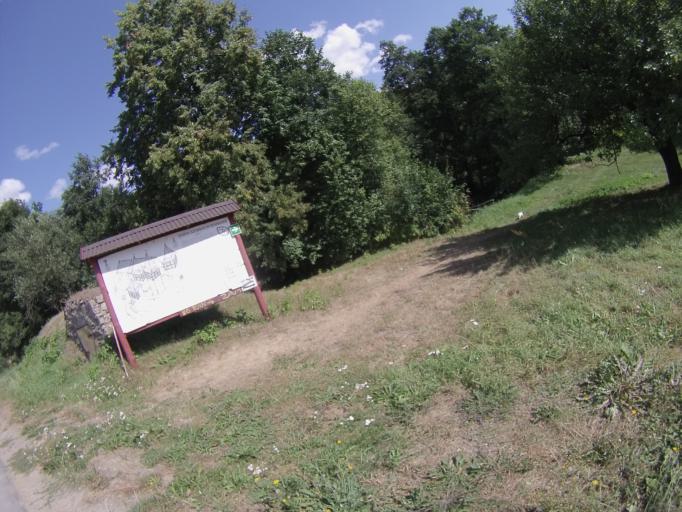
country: PL
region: Swietokrzyskie
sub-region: Powiat kielecki
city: Rakow
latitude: 50.7106
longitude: 21.0463
